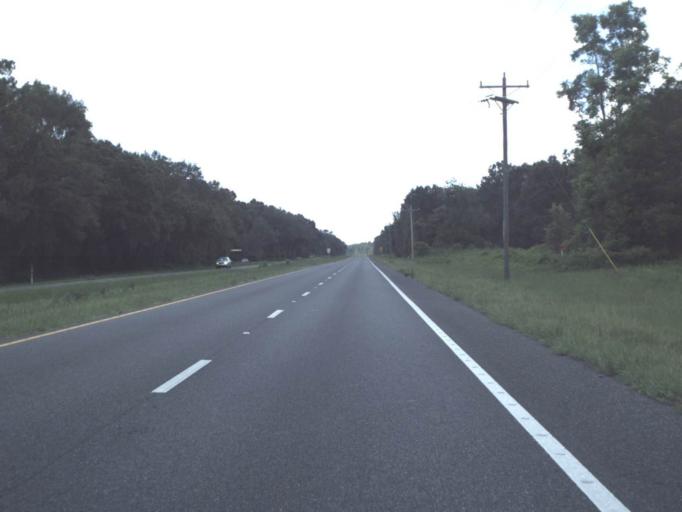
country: US
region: Florida
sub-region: Taylor County
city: Perry
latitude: 30.1760
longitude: -83.6344
